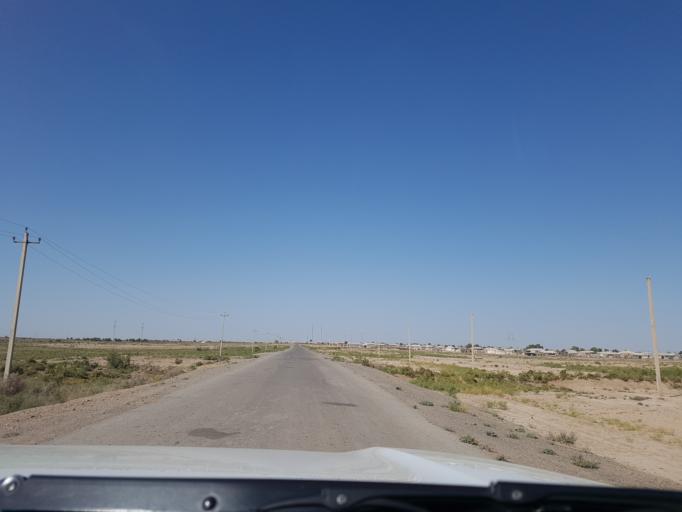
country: IR
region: Razavi Khorasan
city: Sarakhs
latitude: 36.5049
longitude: 61.2535
